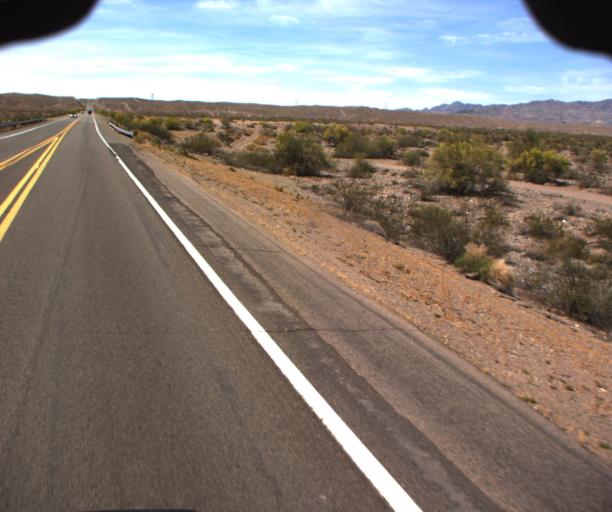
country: US
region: Arizona
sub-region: Mohave County
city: Lake Havasu City
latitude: 34.4172
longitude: -114.1971
